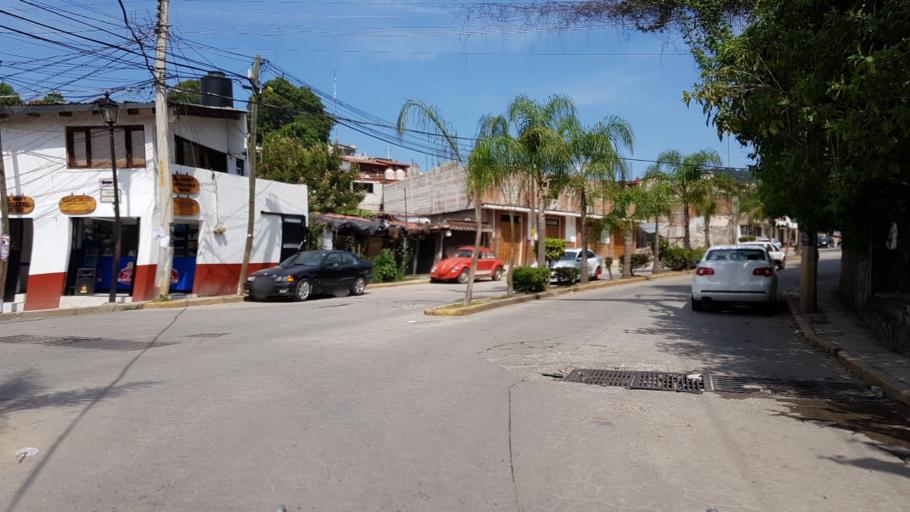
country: MX
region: Mexico
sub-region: Valle de Bravo
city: Colonia Rincon Villa del Valle
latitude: 19.2030
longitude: -100.1262
